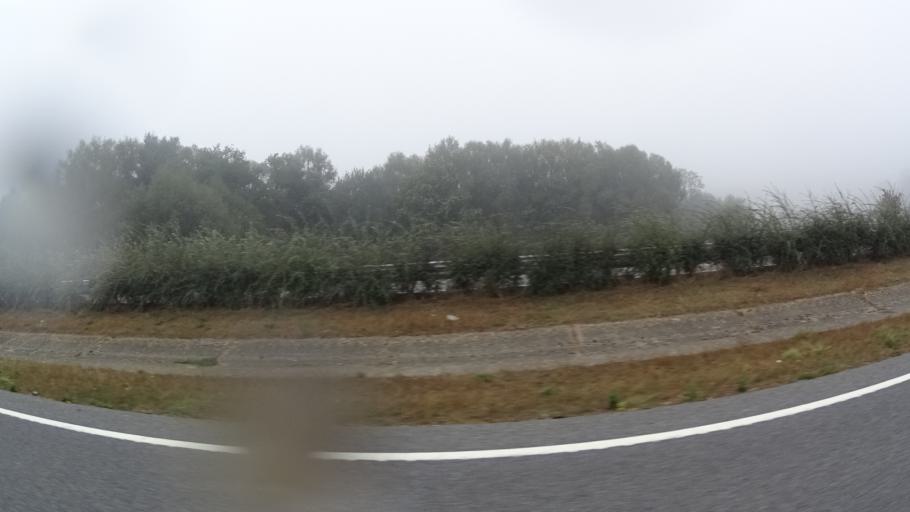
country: ES
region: Galicia
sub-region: Provincia de Lugo
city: Lugo
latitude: 42.9846
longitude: -7.5013
